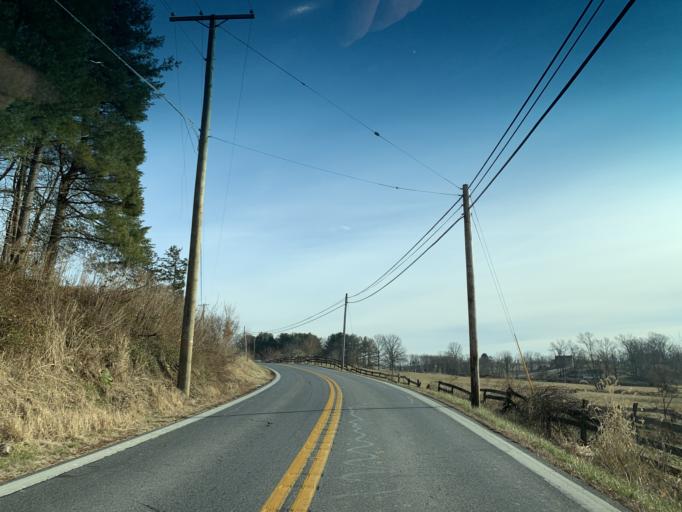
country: US
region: Maryland
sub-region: Carroll County
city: Hampstead
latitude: 39.6046
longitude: -76.7955
